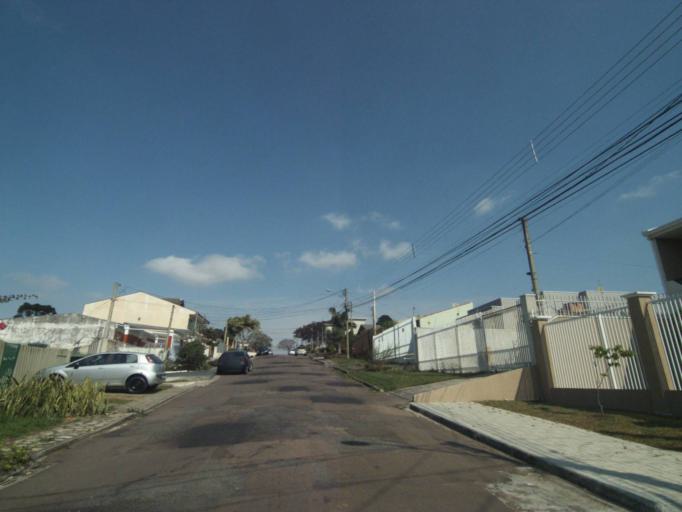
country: BR
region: Parana
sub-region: Curitiba
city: Curitiba
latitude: -25.4817
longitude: -49.3267
